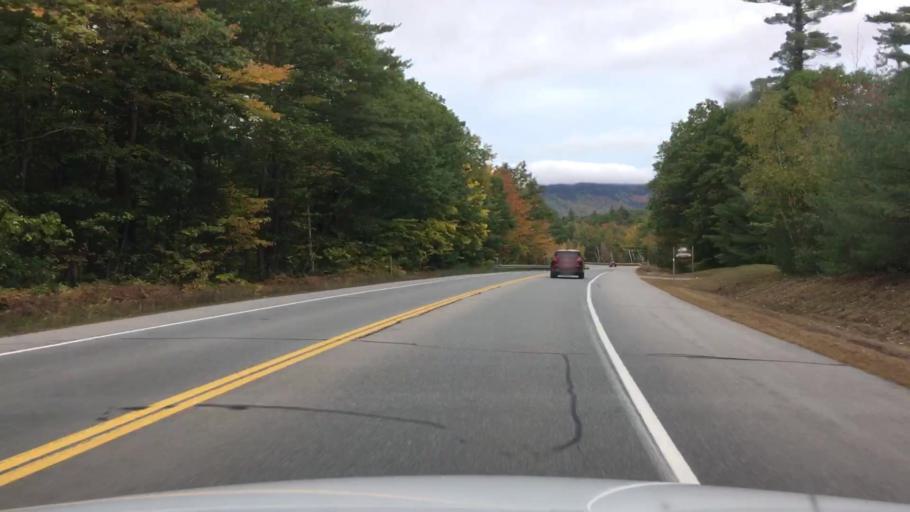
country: US
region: New Hampshire
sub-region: Coos County
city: Gorham
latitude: 44.3903
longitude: -71.0319
